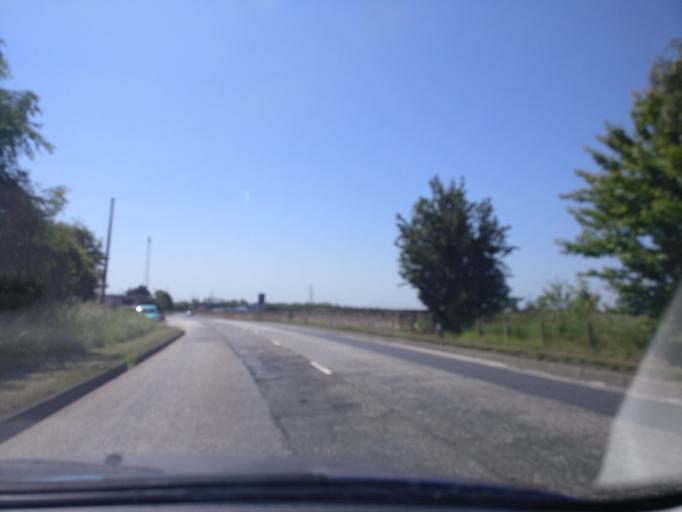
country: GB
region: Scotland
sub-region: East Lothian
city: Tranent
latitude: 55.9617
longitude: -2.9420
